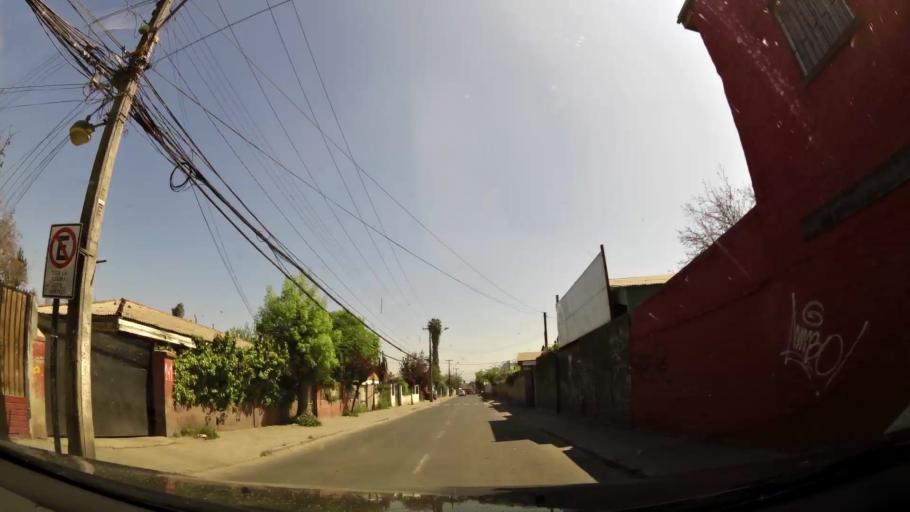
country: CL
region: Santiago Metropolitan
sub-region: Provincia de Santiago
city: Lo Prado
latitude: -33.3691
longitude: -70.7364
